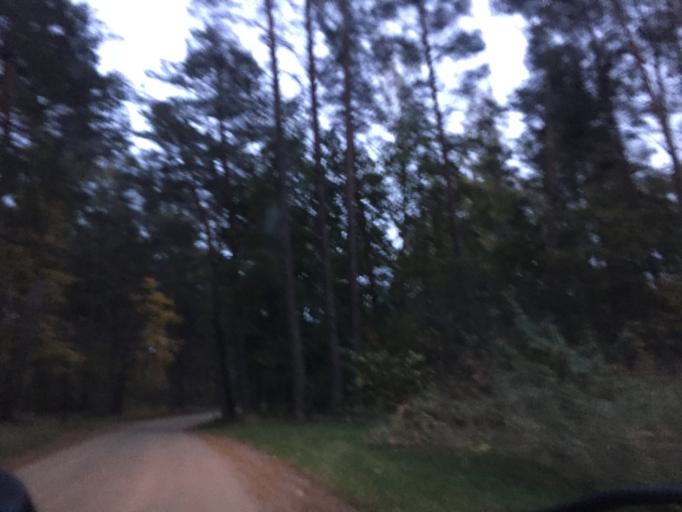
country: LV
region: Adazi
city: Adazi
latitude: 57.0857
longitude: 24.3491
